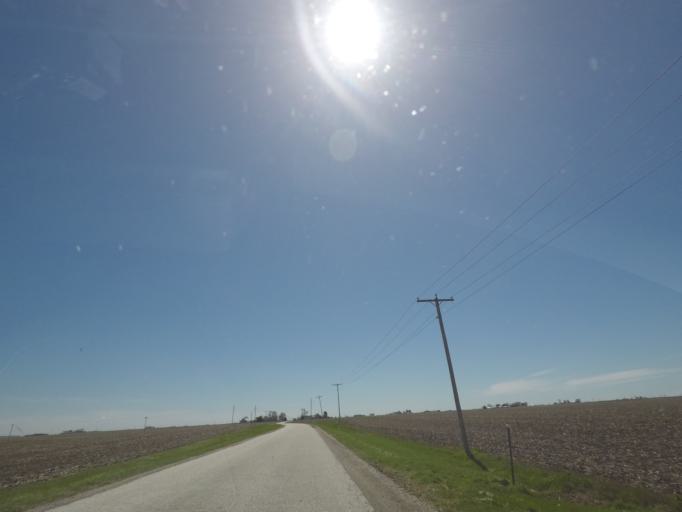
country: US
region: Illinois
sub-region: Logan County
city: Mount Pulaski
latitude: 40.0504
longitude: -89.1824
